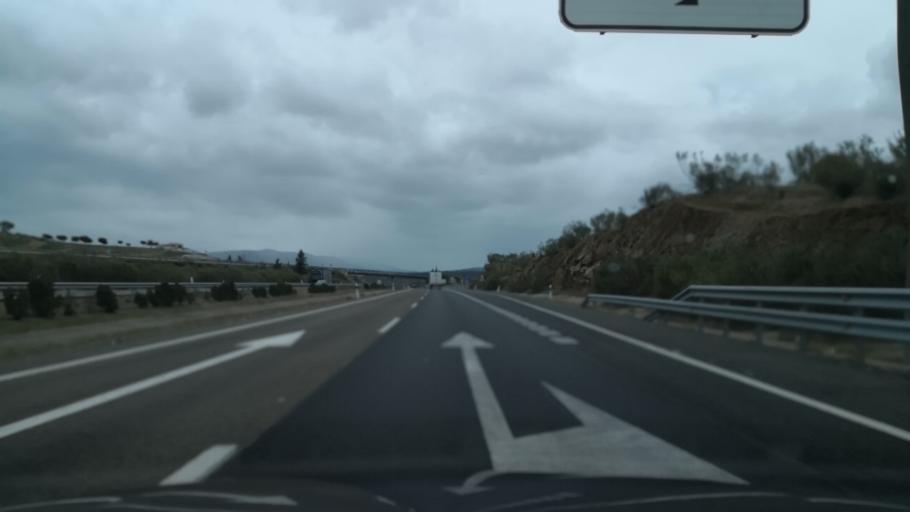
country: ES
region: Extremadura
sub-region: Provincia de Caceres
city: Galisteo
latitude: 39.9247
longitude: -6.2337
